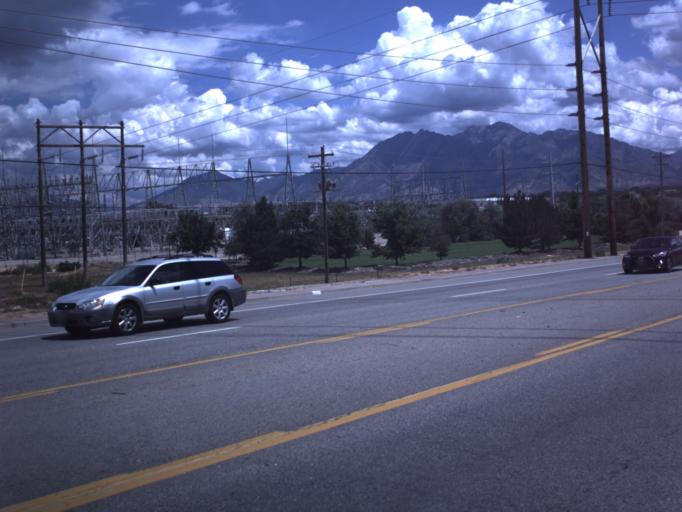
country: US
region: Utah
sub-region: Salt Lake County
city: South Jordan
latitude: 40.5877
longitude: -111.9172
